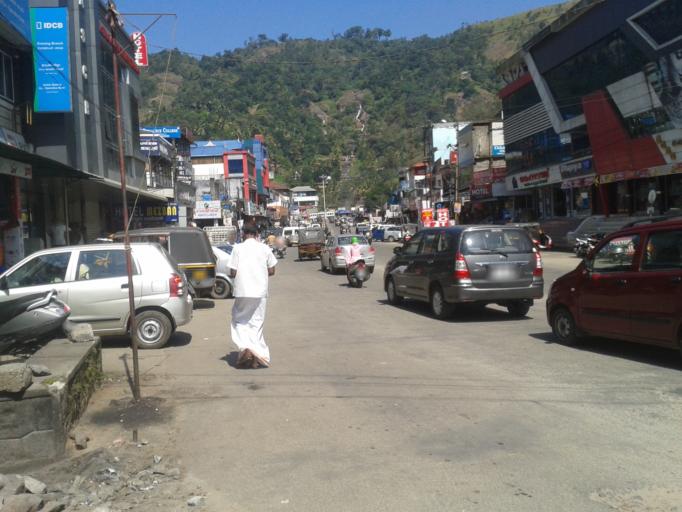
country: IN
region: Kerala
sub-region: Idukki
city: Munnar
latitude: 10.0119
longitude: 76.9555
